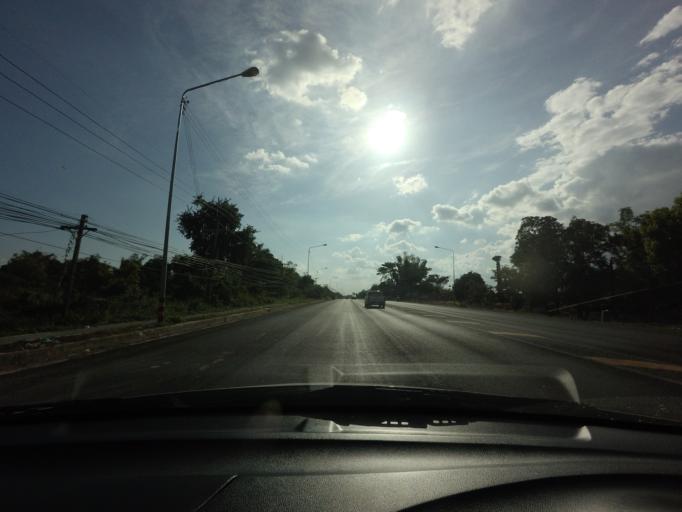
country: TH
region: Nakhon Nayok
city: Nakhon Nayok
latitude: 14.2529
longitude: 101.2588
